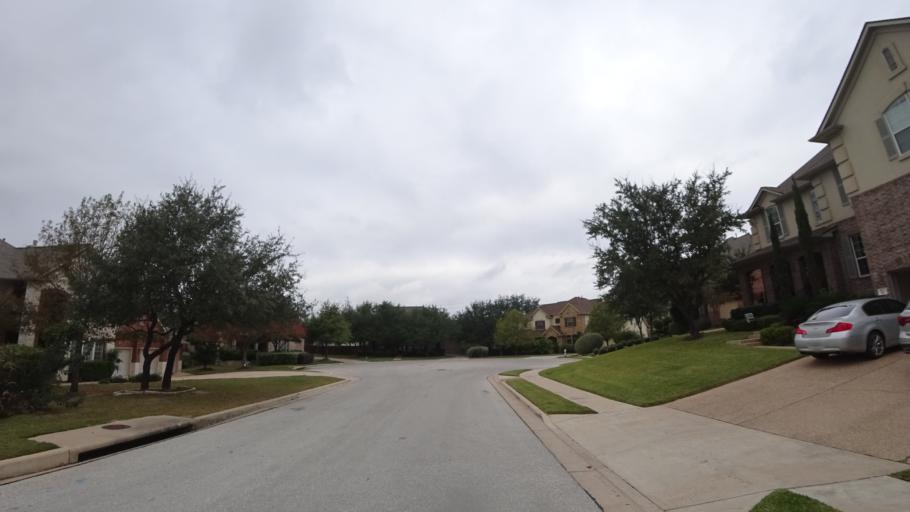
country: US
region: Texas
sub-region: Travis County
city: Hudson Bend
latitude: 30.3581
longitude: -97.9039
